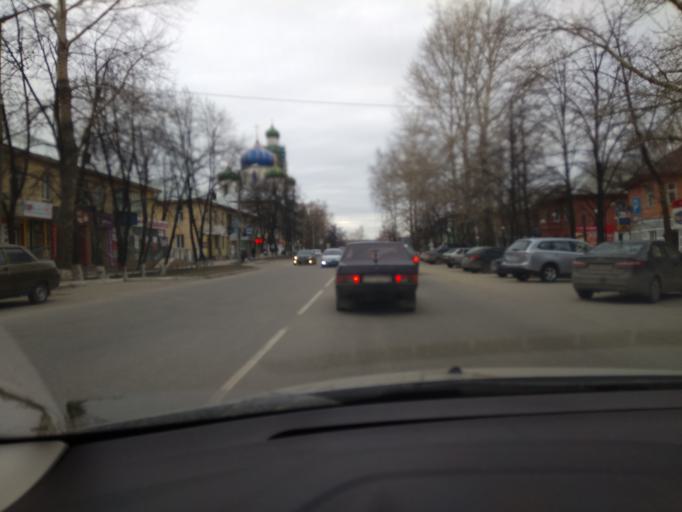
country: RU
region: Chelyabinsk
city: Kyshtym
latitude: 55.7066
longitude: 60.5531
